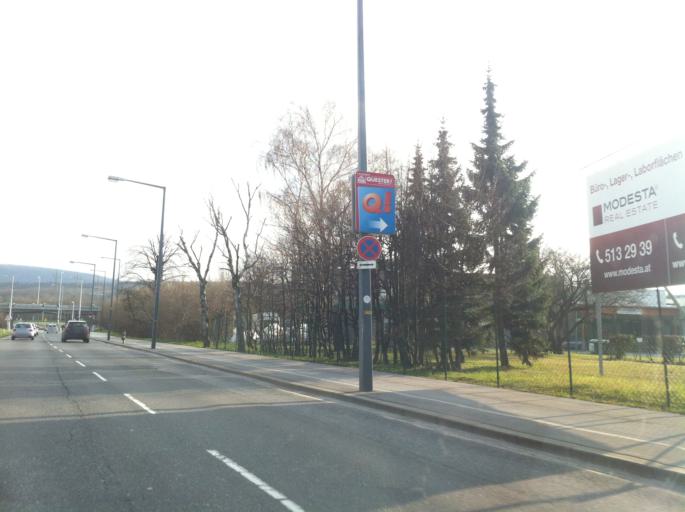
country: AT
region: Lower Austria
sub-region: Politischer Bezirk Wien-Umgebung
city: Purkersdorf
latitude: 48.2068
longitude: 16.2221
